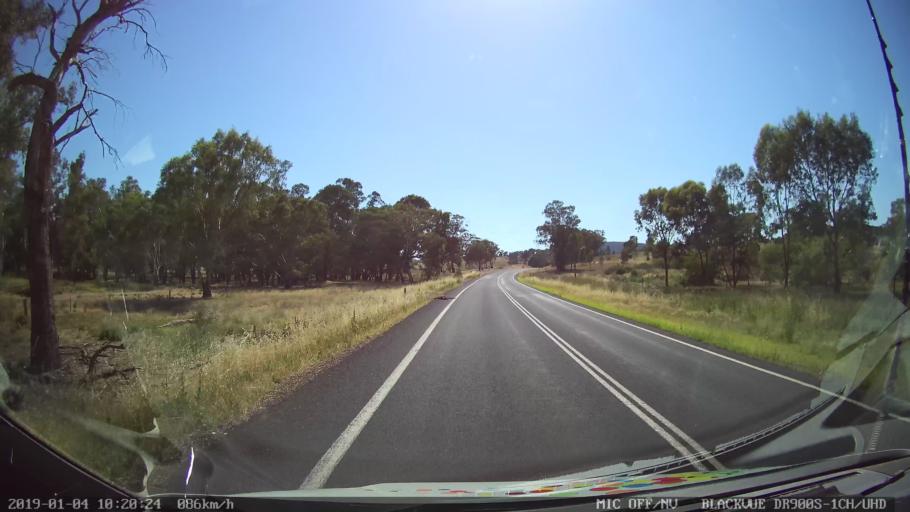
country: AU
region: New South Wales
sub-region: Cabonne
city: Canowindra
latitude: -33.3722
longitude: 148.4951
